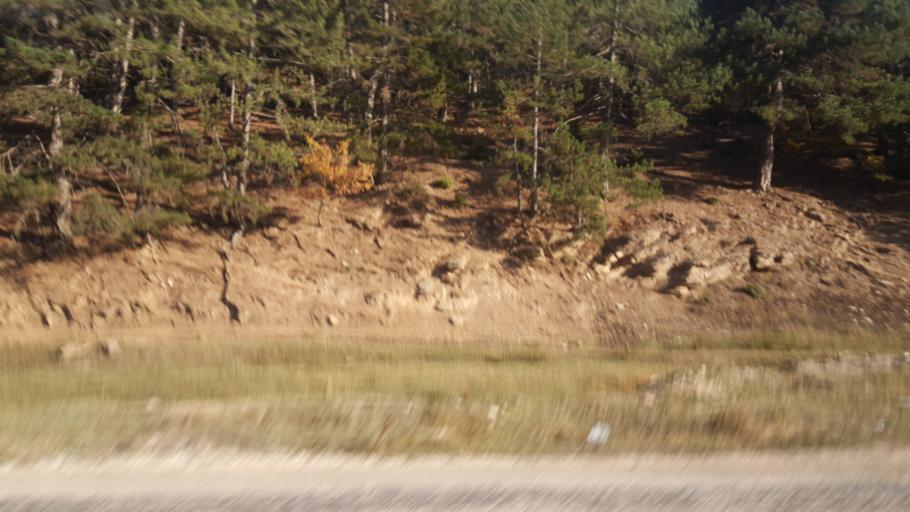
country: TR
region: Eskisehir
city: Kirka
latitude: 39.1089
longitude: 30.5840
